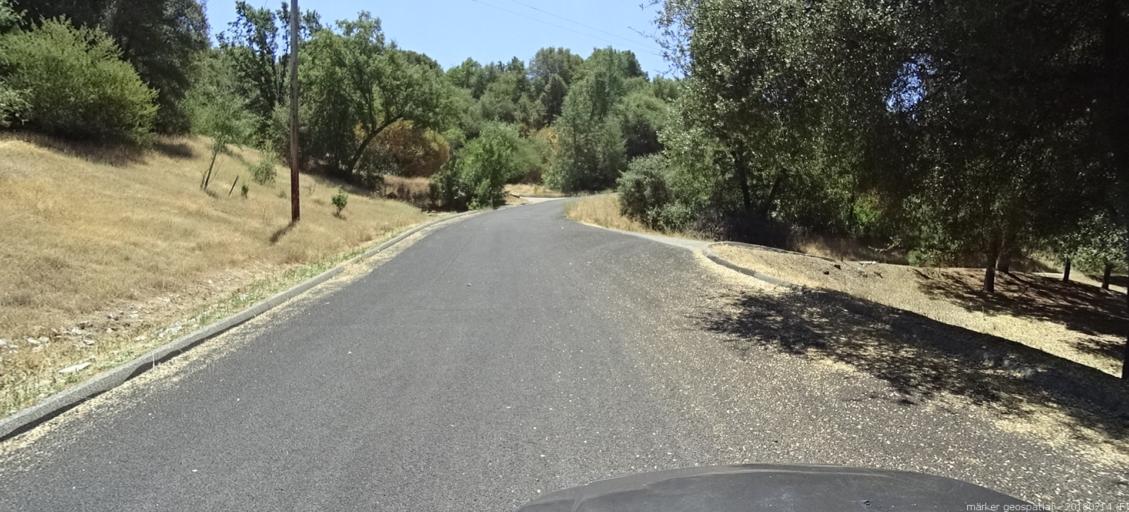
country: US
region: California
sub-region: Madera County
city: Ahwahnee
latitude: 37.3929
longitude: -119.7167
